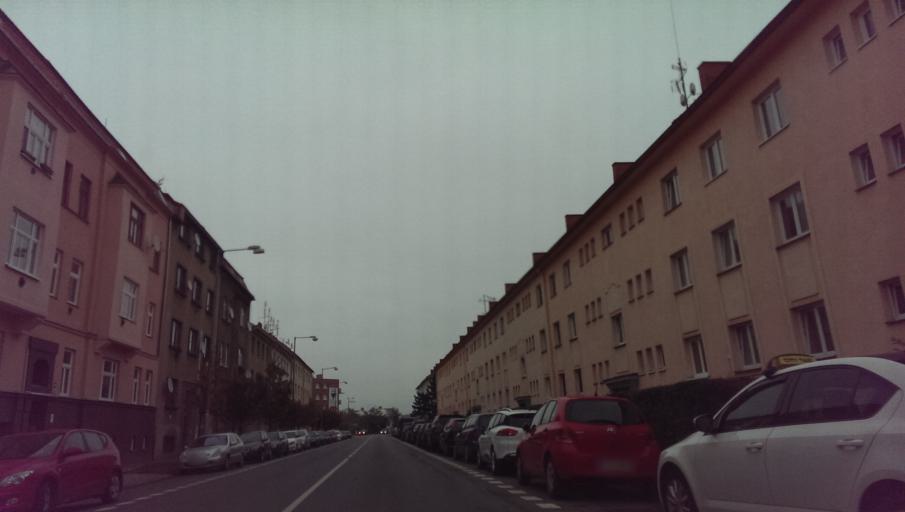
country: CZ
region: South Moravian
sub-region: Okres Znojmo
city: Znojmo
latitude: 48.8571
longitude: 16.0612
